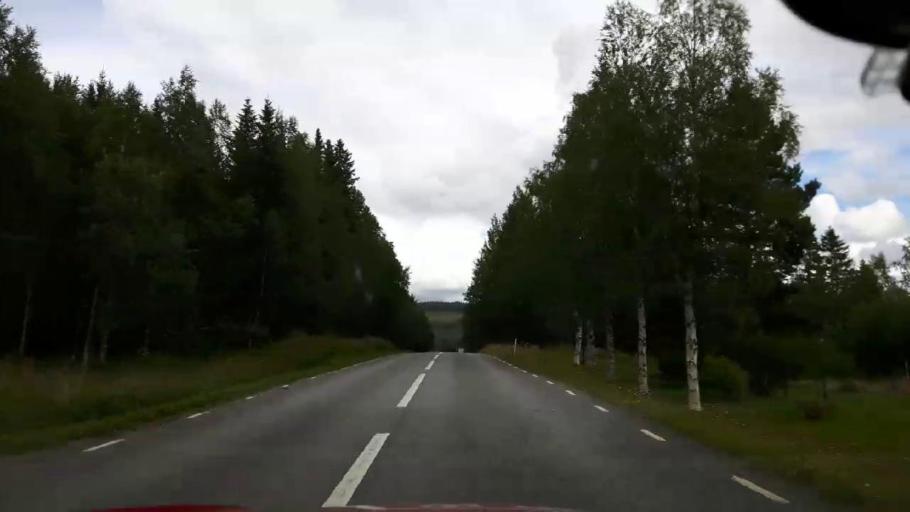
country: NO
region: Nord-Trondelag
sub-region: Lierne
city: Sandvika
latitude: 64.3923
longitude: 14.4785
